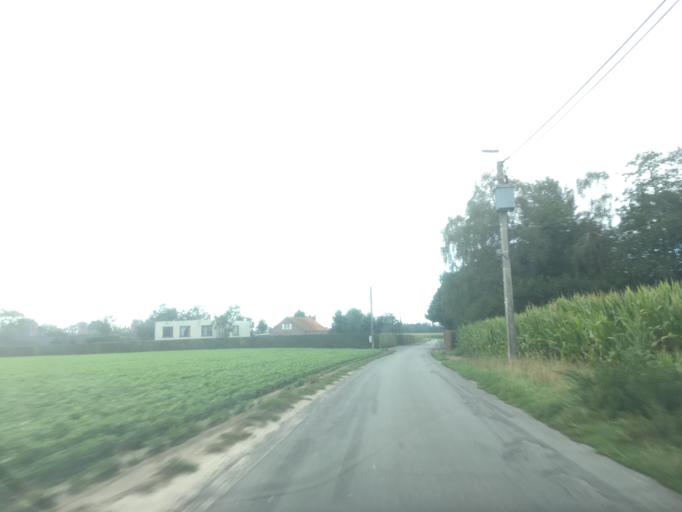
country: BE
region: Flanders
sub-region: Provincie West-Vlaanderen
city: Ardooie
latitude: 50.9969
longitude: 3.1997
